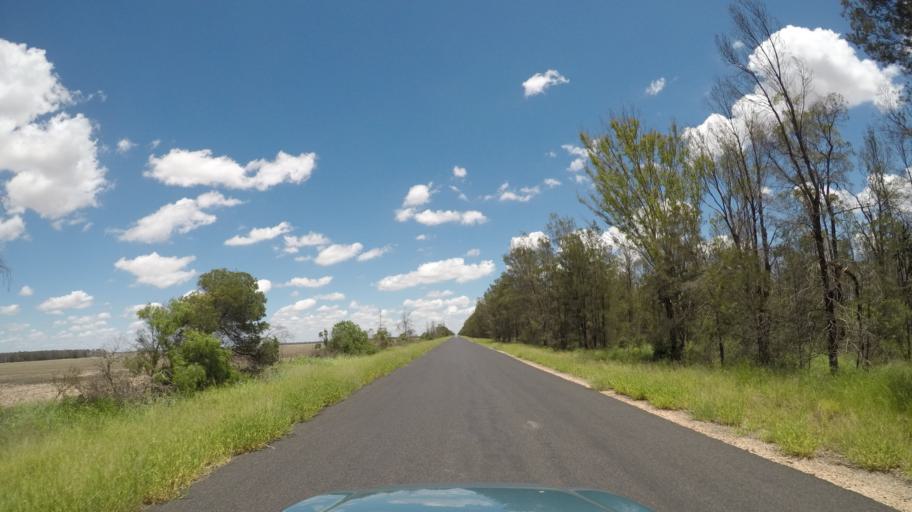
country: AU
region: Queensland
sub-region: Goondiwindi
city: Goondiwindi
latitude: -28.1655
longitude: 150.4374
